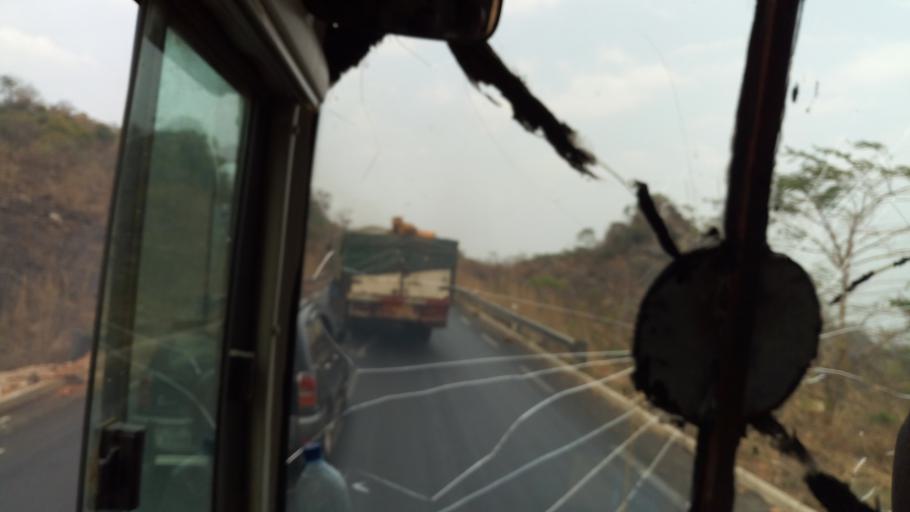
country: TG
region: Kara
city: Bafilo
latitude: 9.2685
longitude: 1.2345
